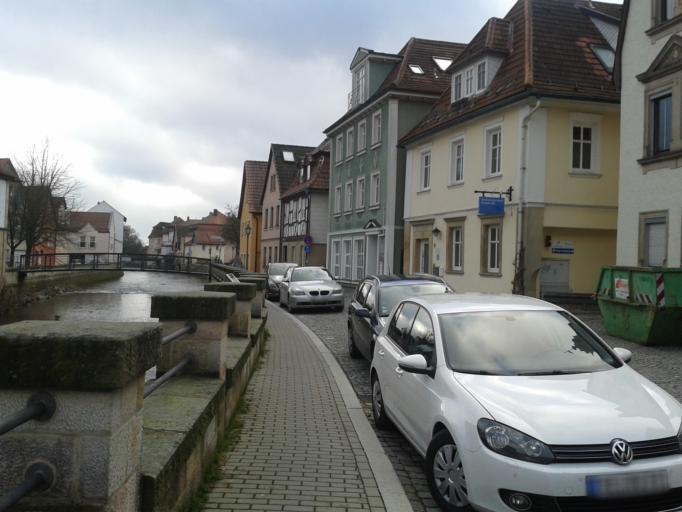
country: DE
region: Bavaria
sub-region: Upper Franconia
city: Kronach
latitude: 50.2411
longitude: 11.3220
